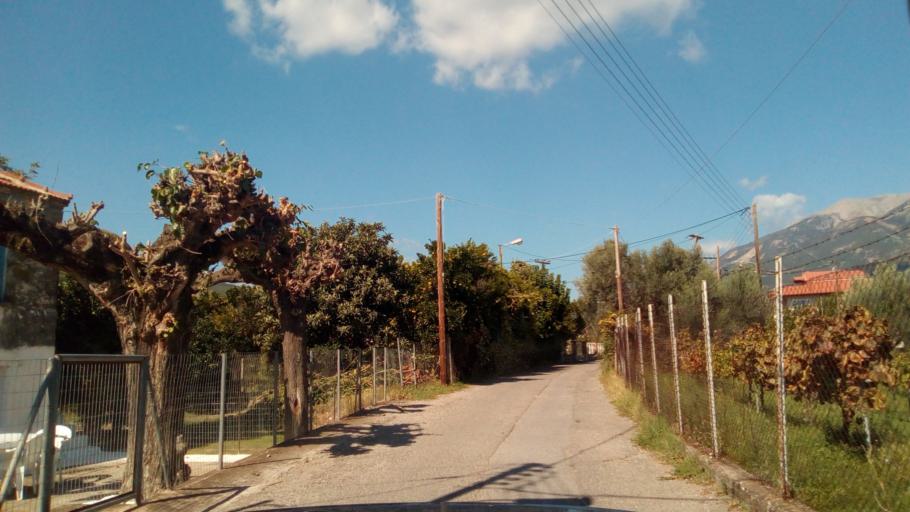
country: GR
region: West Greece
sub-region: Nomos Aitolias kai Akarnanias
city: Nafpaktos
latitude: 38.3871
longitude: 21.8012
